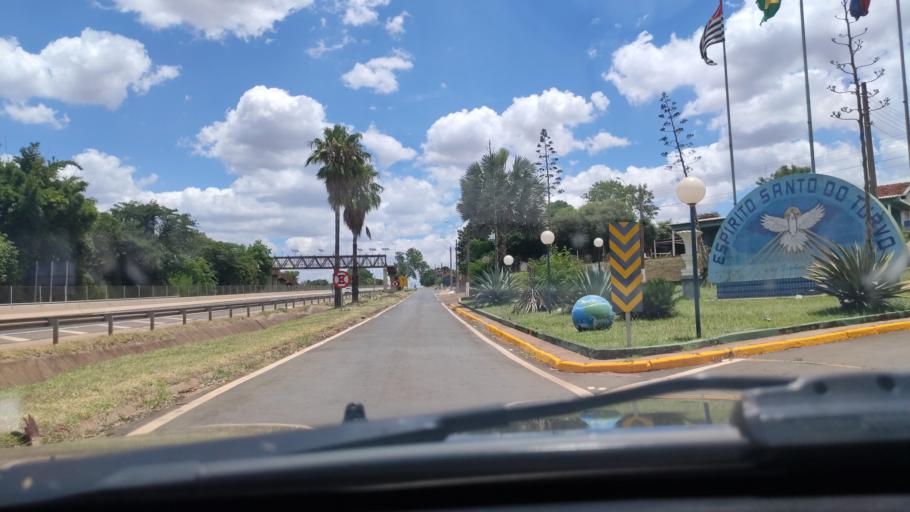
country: BR
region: Sao Paulo
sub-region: Duartina
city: Duartina
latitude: -22.6970
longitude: -49.4288
